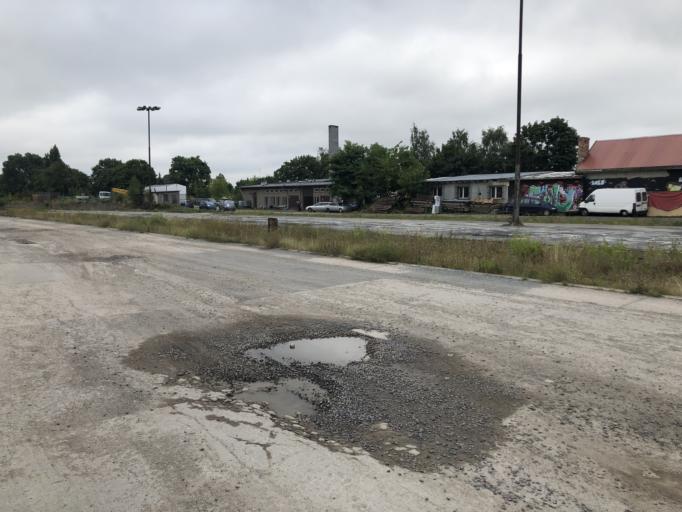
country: PL
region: Warmian-Masurian Voivodeship
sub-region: Powiat olsztynski
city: Olsztyn
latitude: 53.7867
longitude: 20.5056
